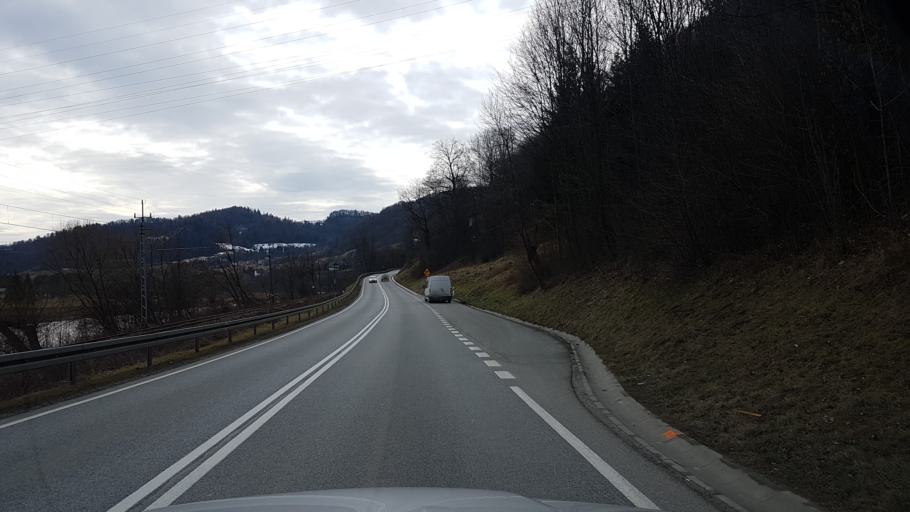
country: PL
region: Lesser Poland Voivodeship
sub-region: Powiat nowosadecki
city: Piwniczna-Zdroj
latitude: 49.4632
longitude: 20.6964
